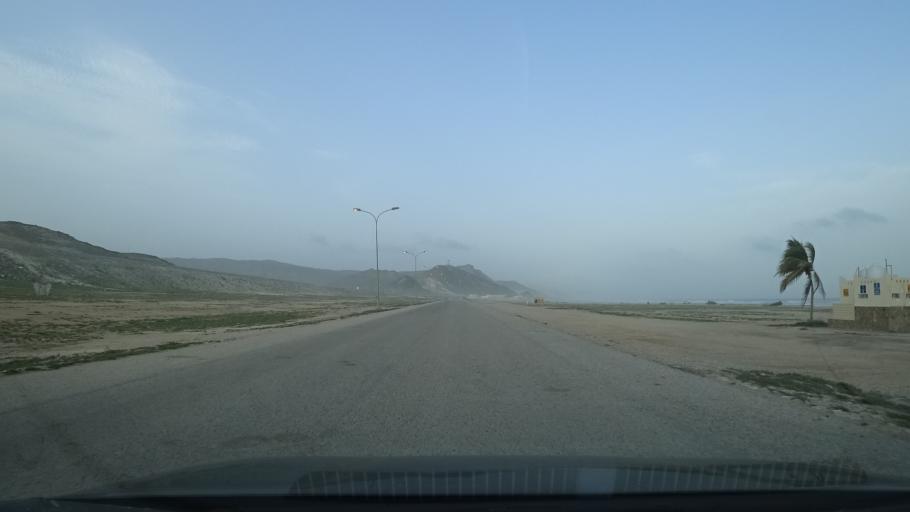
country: OM
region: Zufar
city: Salalah
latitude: 16.8790
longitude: 53.7706
